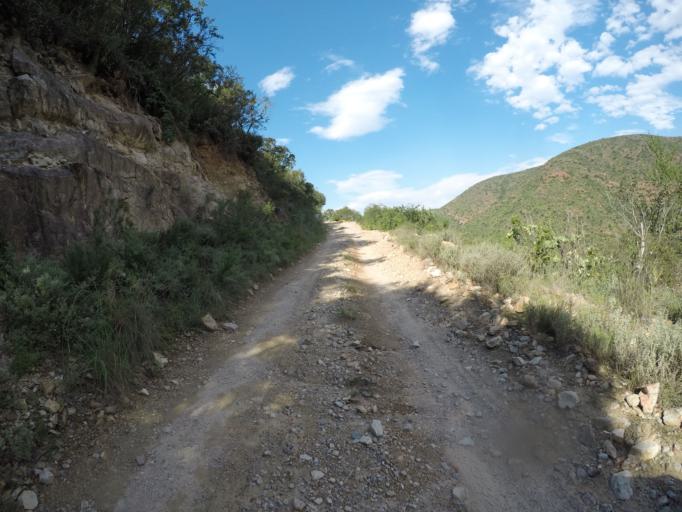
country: ZA
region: Eastern Cape
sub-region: Cacadu District Municipality
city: Kareedouw
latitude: -33.6505
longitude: 24.3479
